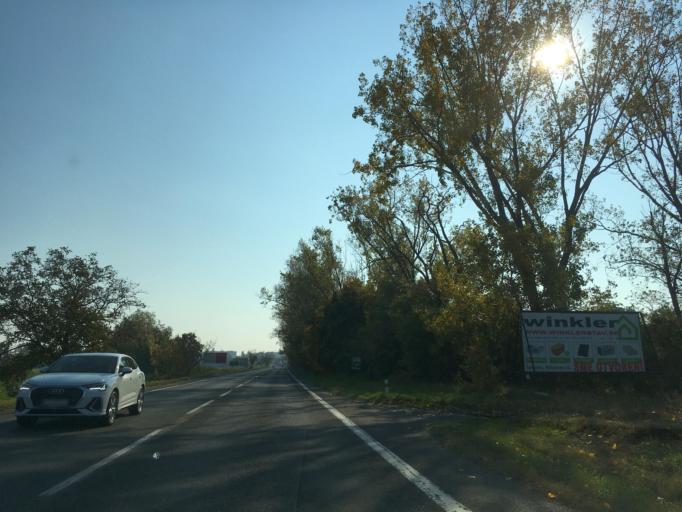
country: SK
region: Trnavsky
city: Samorin
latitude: 48.0403
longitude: 17.2990
